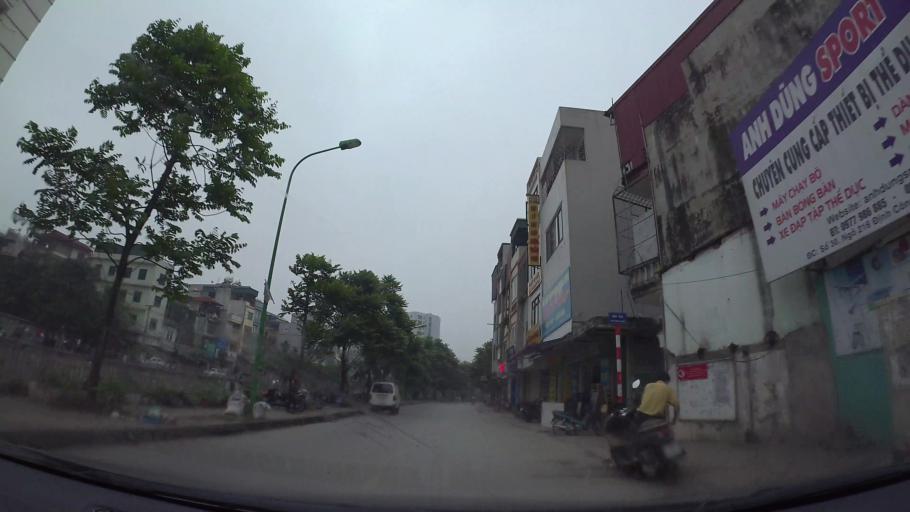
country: VN
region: Ha Noi
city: Hai BaTrung
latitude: 20.9854
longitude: 105.8349
